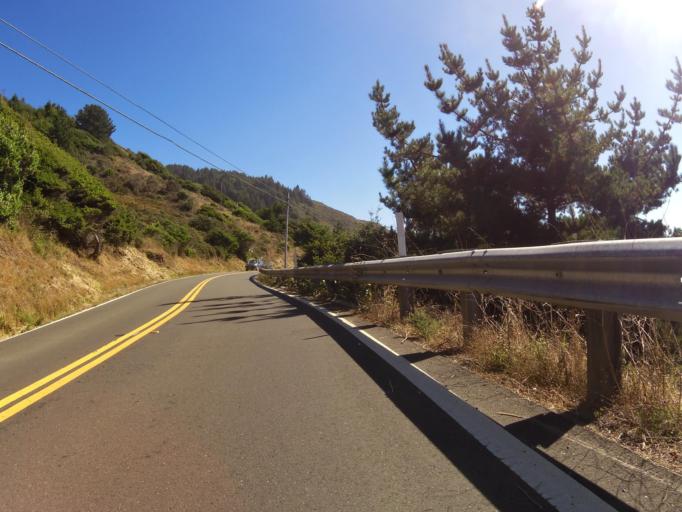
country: US
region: California
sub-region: Mendocino County
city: Fort Bragg
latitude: 39.6250
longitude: -123.7825
